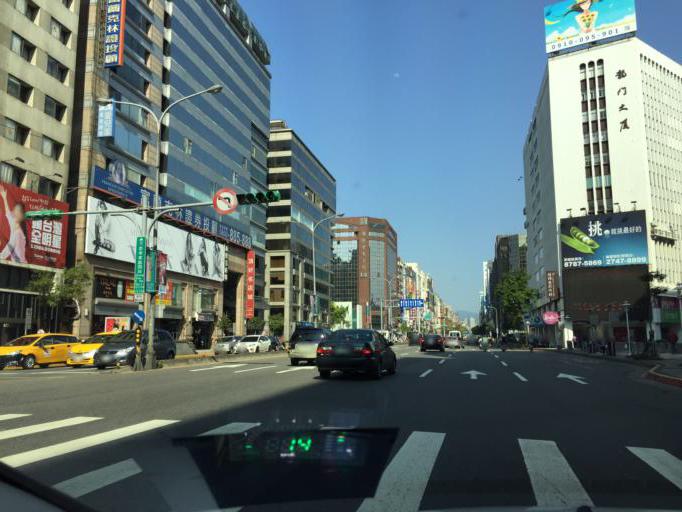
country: TW
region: Taipei
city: Taipei
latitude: 25.0415
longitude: 121.5472
